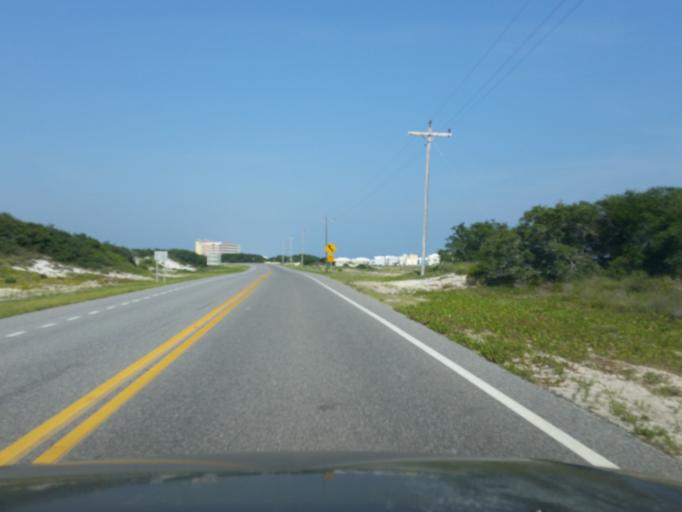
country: US
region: Alabama
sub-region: Mobile County
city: Dauphin Island
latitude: 30.2293
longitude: -88.0062
